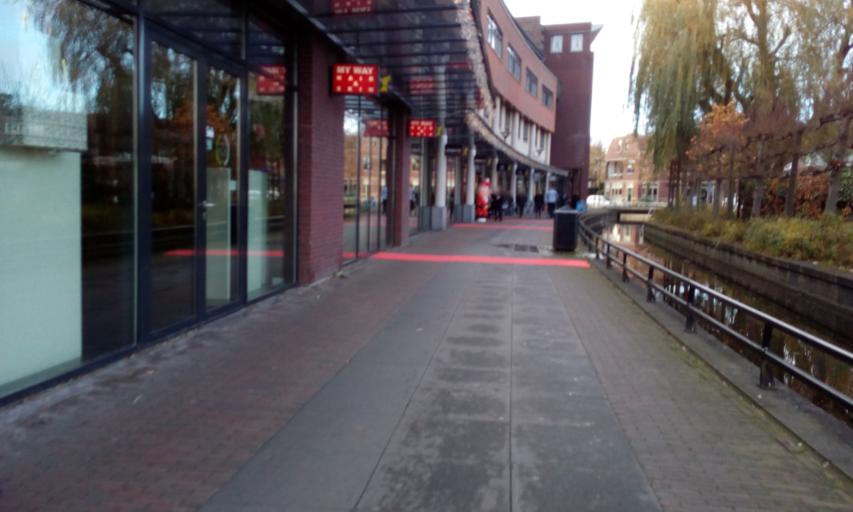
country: NL
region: South Holland
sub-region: Gemeente Lansingerland
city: Bergschenhoek
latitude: 51.9887
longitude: 4.5013
